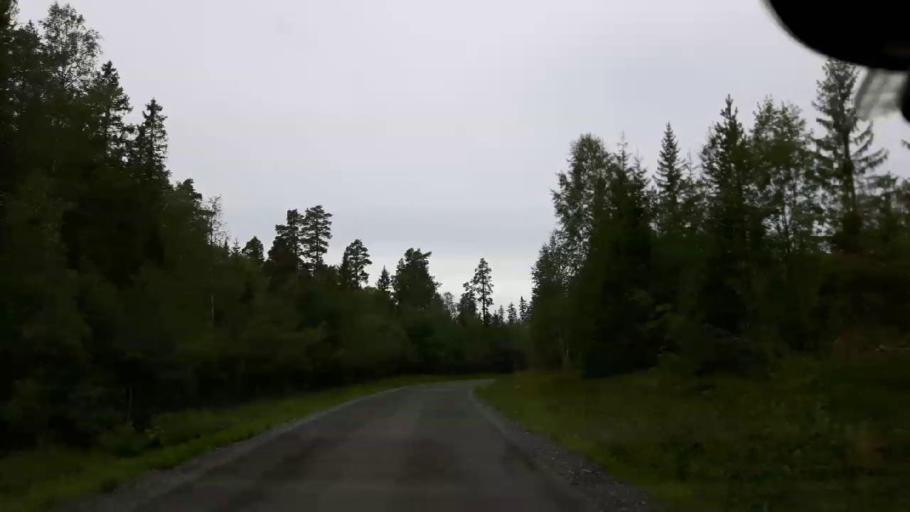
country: SE
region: Jaemtland
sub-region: Krokoms Kommun
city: Krokom
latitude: 63.2896
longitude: 14.3801
